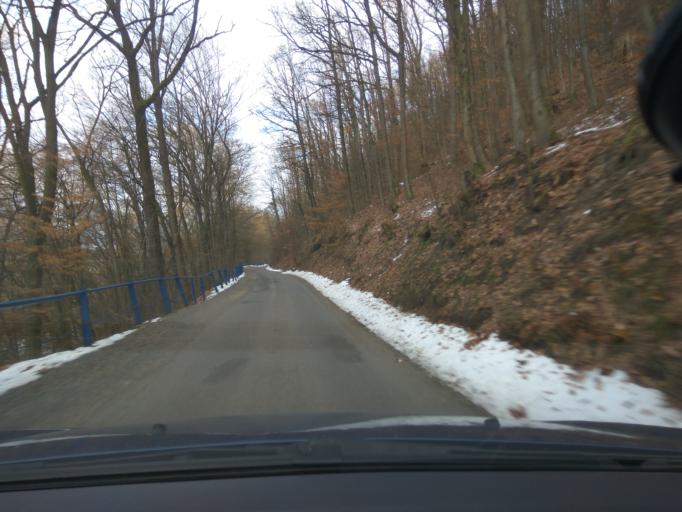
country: SK
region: Banskobystricky
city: Zarnovica
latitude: 48.4749
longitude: 18.7346
